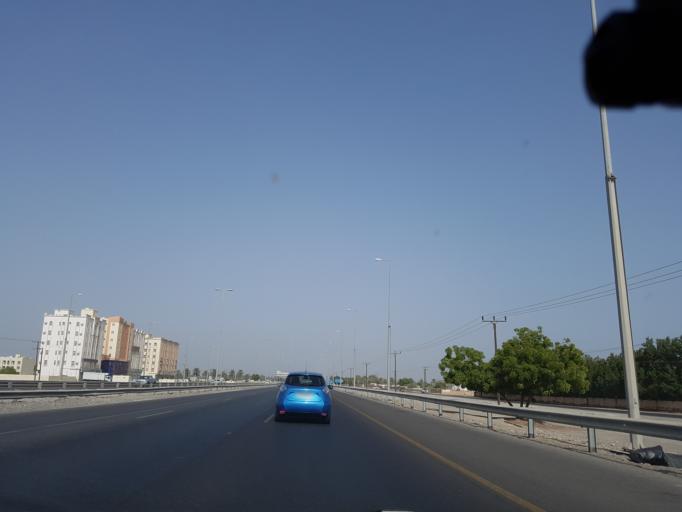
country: OM
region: Al Batinah
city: Barka'
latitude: 23.6702
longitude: 57.8716
